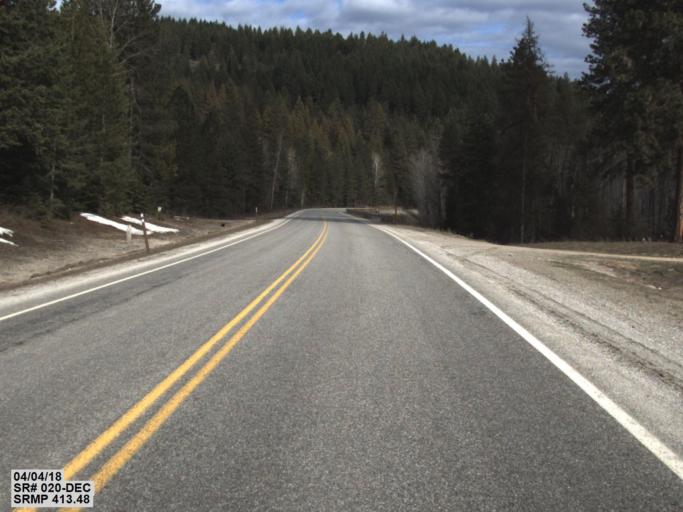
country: US
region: Washington
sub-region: Pend Oreille County
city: Newport
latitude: 48.4157
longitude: -117.3160
